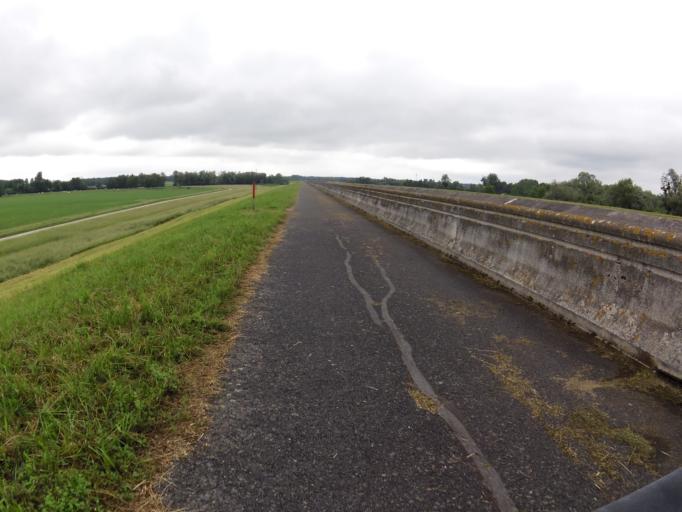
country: FR
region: Champagne-Ardenne
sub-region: Departement de la Haute-Marne
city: Villiers-en-Lieu
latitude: 48.5854
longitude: 4.8543
